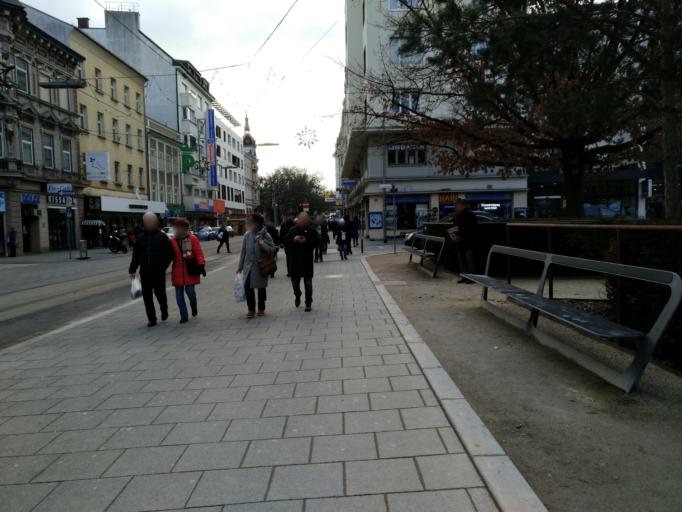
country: AT
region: Upper Austria
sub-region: Linz Stadt
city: Linz
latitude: 48.2975
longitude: 14.2916
